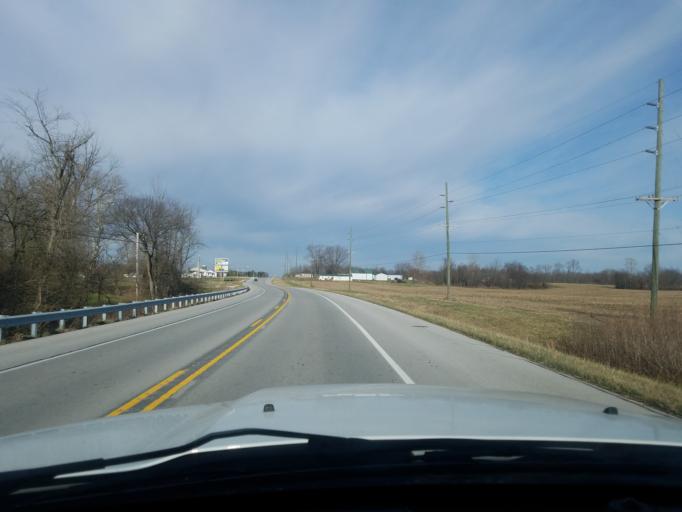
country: US
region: Indiana
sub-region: Orange County
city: Paoli
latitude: 38.6027
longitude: -86.4576
